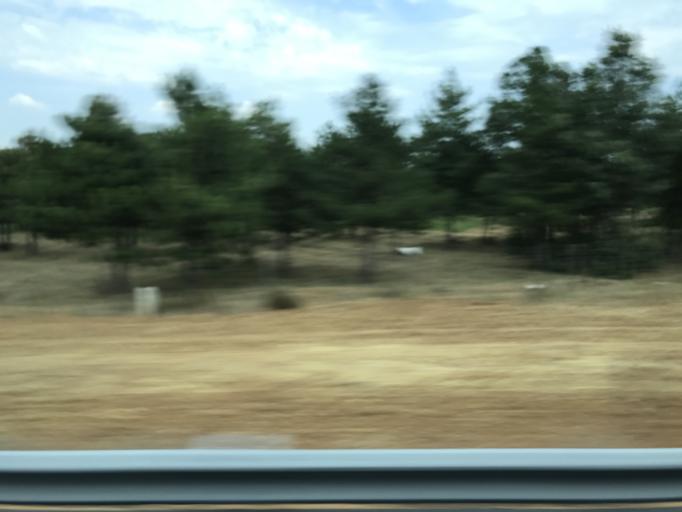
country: ES
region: Castille and Leon
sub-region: Provincia de Segovia
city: Castillejo de Mesleon
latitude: 41.3055
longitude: -3.6081
